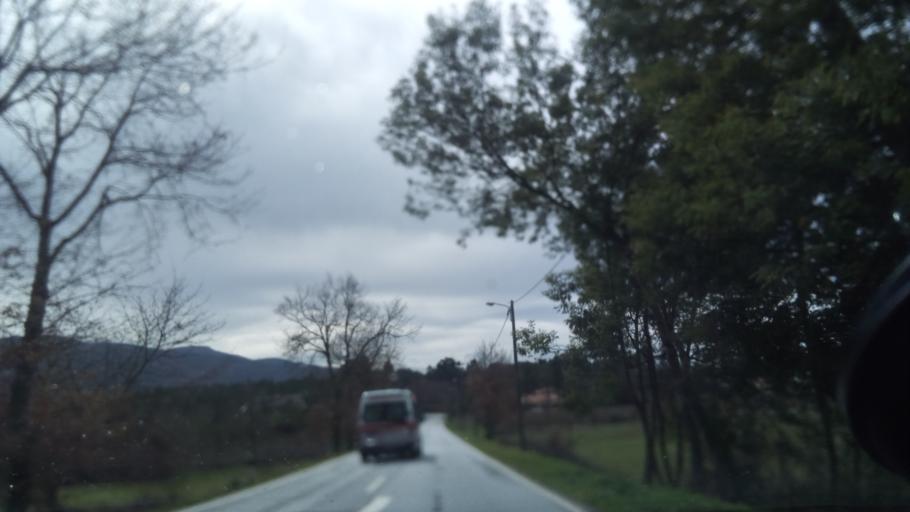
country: PT
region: Guarda
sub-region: Seia
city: Seia
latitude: 40.4472
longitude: -7.7105
